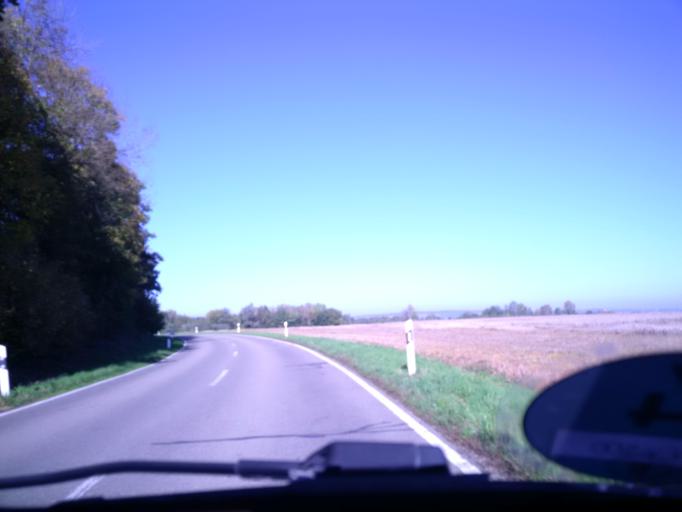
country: DE
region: Baden-Wuerttemberg
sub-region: Tuebingen Region
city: Huttisheim
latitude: 48.3150
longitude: 9.9403
